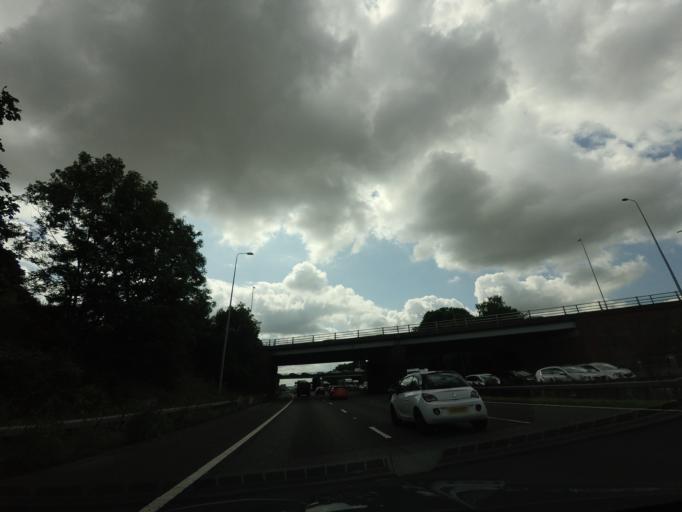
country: GB
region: England
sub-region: Borough of Wigan
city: Shevington
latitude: 53.5905
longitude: -2.6942
